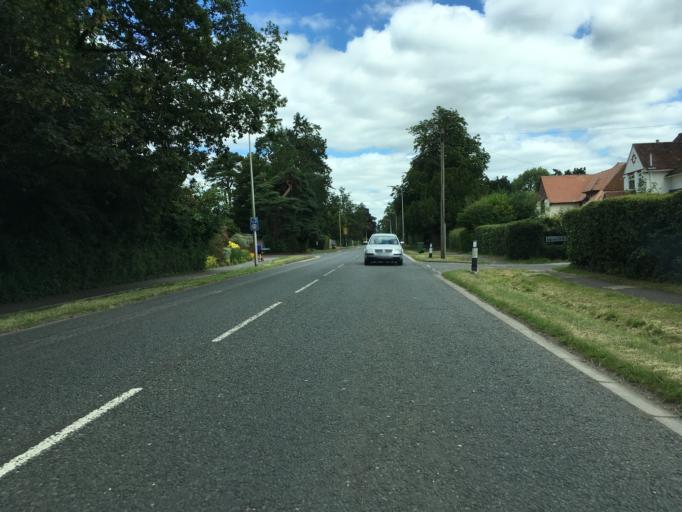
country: GB
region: England
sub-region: West Berkshire
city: Newbury
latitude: 51.3768
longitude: -1.3438
